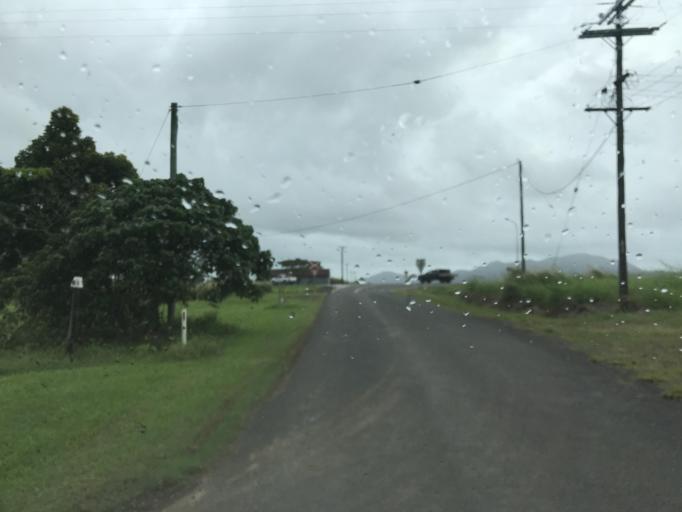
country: AU
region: Queensland
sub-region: Cassowary Coast
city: Innisfail
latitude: -17.4813
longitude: 145.9894
